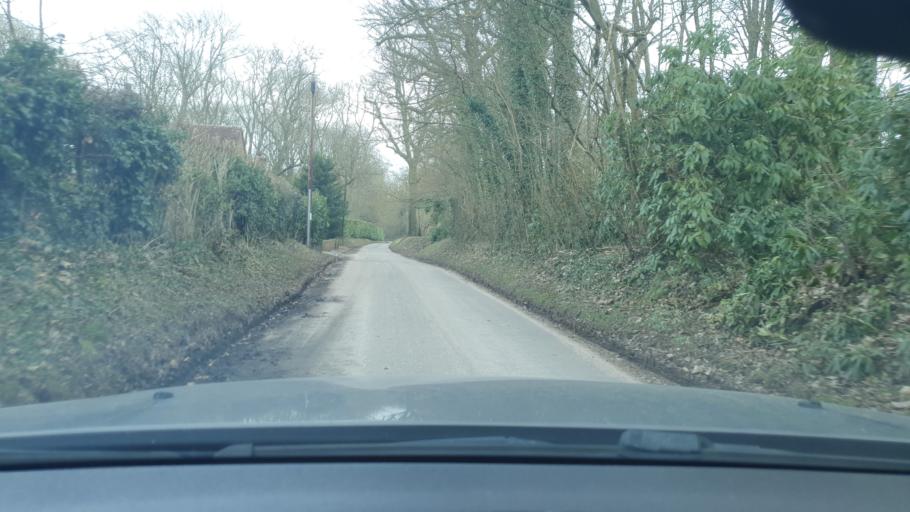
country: GB
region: England
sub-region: Wiltshire
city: Shalbourne
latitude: 51.3680
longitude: -1.5029
